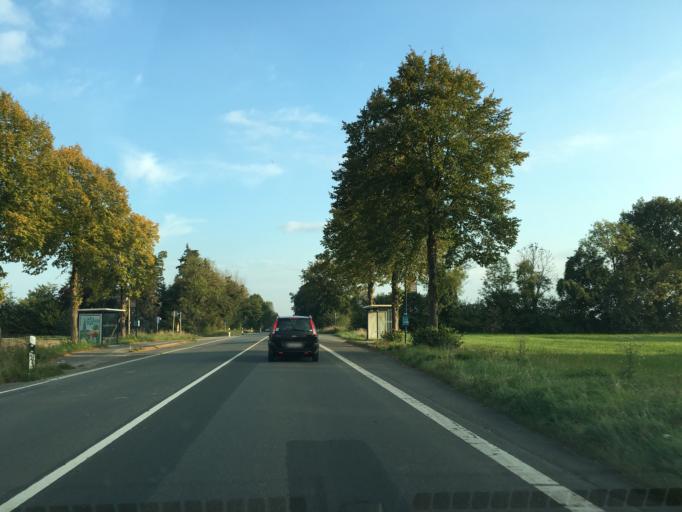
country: DE
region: North Rhine-Westphalia
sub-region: Regierungsbezirk Munster
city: Altenberge
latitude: 52.0328
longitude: 7.4820
